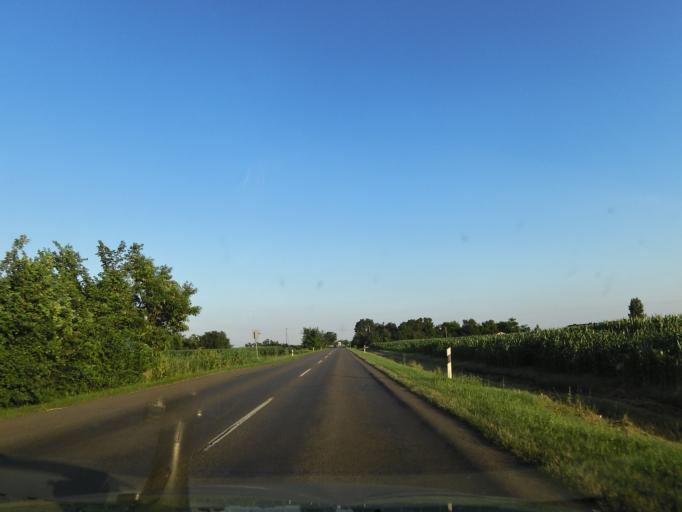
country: HU
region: Csongrad
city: Szegvar
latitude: 46.5751
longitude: 20.3054
